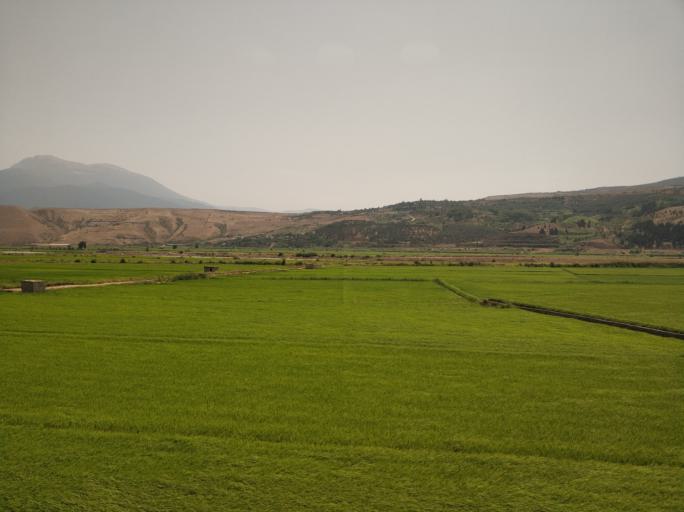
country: IR
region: Gilan
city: Pa'in-e Bazar-e Rudbar
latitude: 36.8772
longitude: 49.4954
